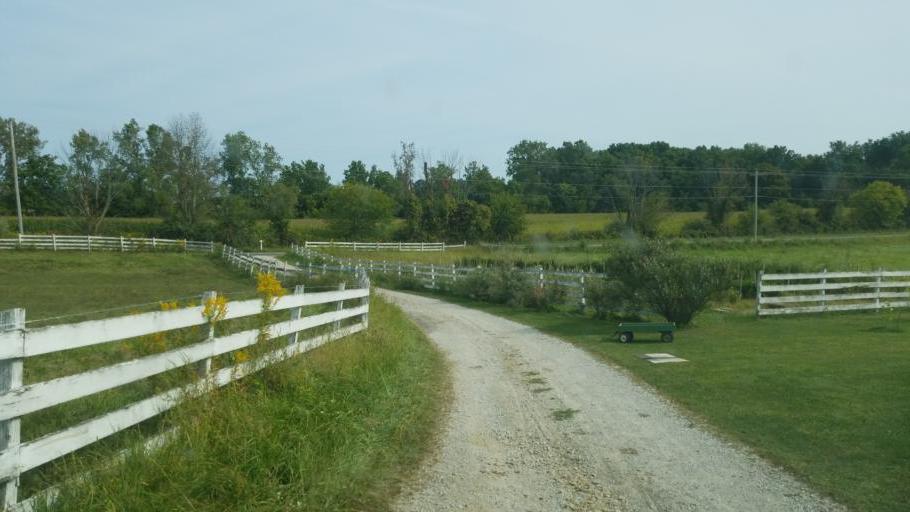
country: US
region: Ohio
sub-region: Knox County
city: Fredericktown
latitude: 40.4943
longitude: -82.5907
